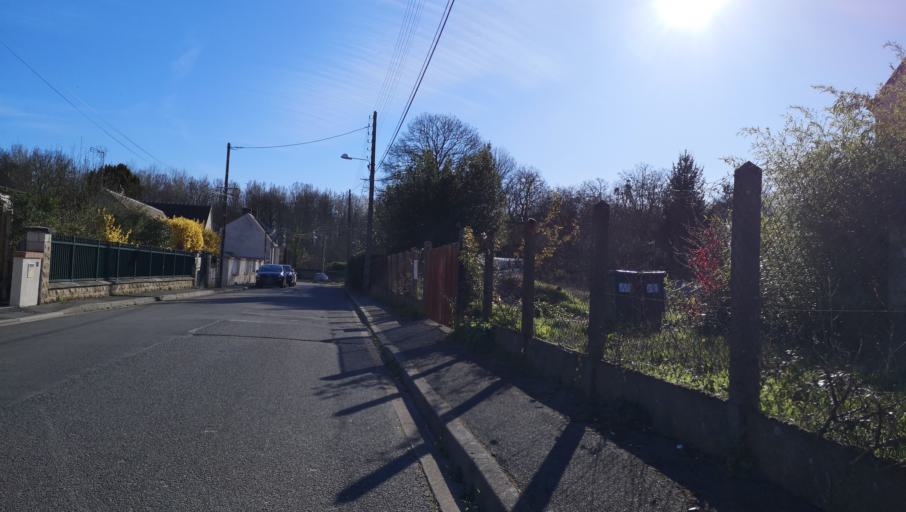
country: FR
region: Centre
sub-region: Departement du Loiret
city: Saint-Jean-de-Braye
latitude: 47.9064
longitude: 1.9898
